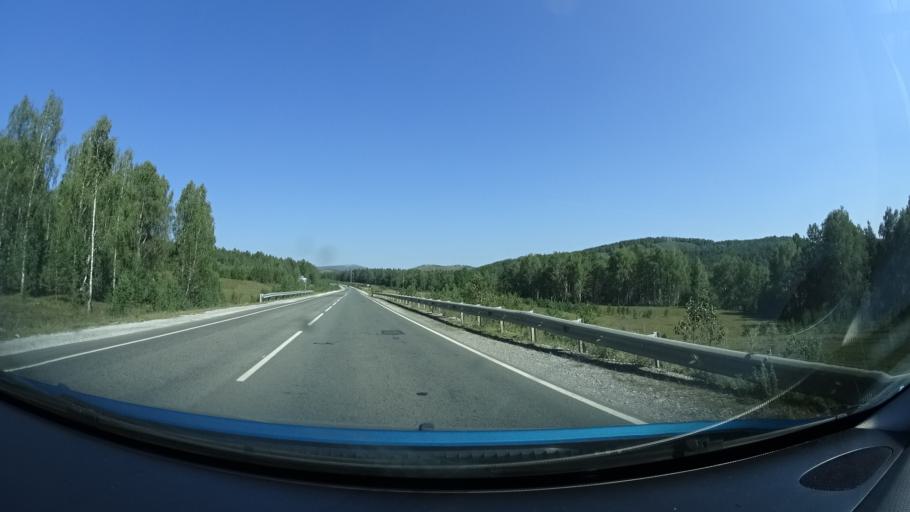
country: RU
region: Bashkortostan
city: Abzakovo
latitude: 53.8463
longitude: 58.5826
